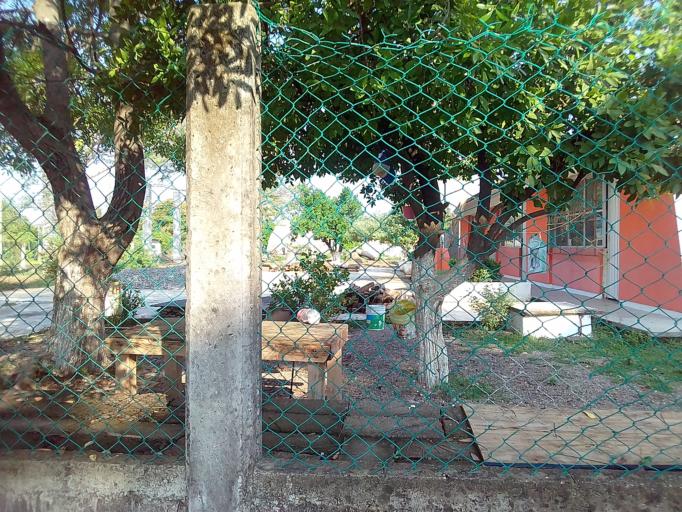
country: MX
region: Oaxaca
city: San Francisco Ixhuatan
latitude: 16.3356
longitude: -94.5214
